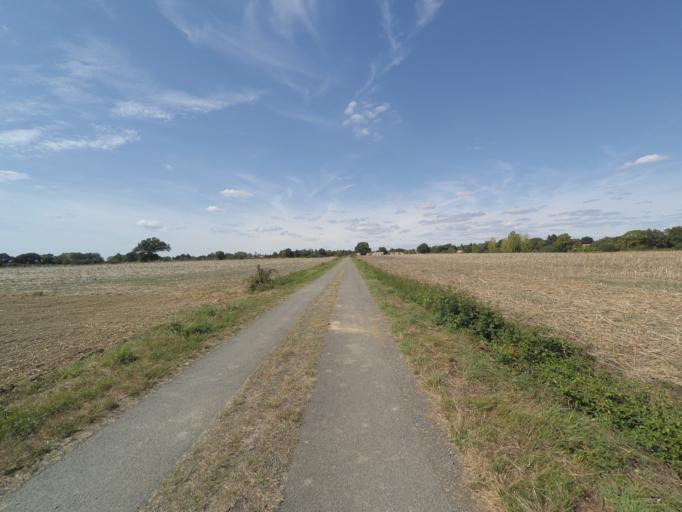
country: FR
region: Pays de la Loire
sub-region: Departement de la Loire-Atlantique
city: Vieillevigne
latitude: 46.9576
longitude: -1.4154
